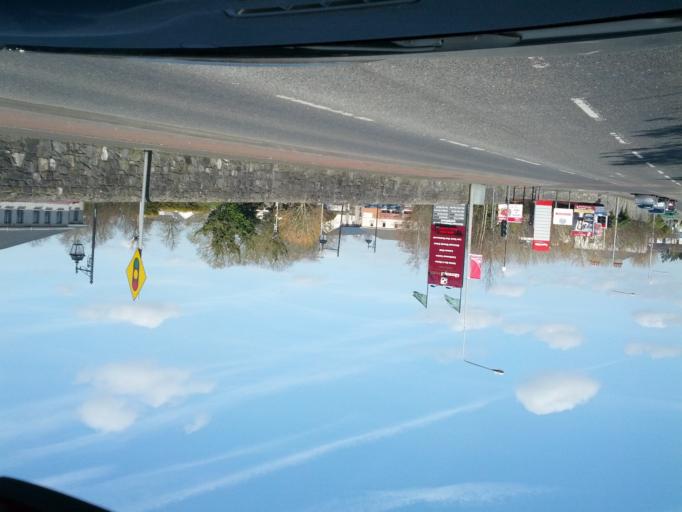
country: IE
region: Leinster
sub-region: Kildare
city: Maynooth
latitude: 53.3798
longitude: -6.5890
